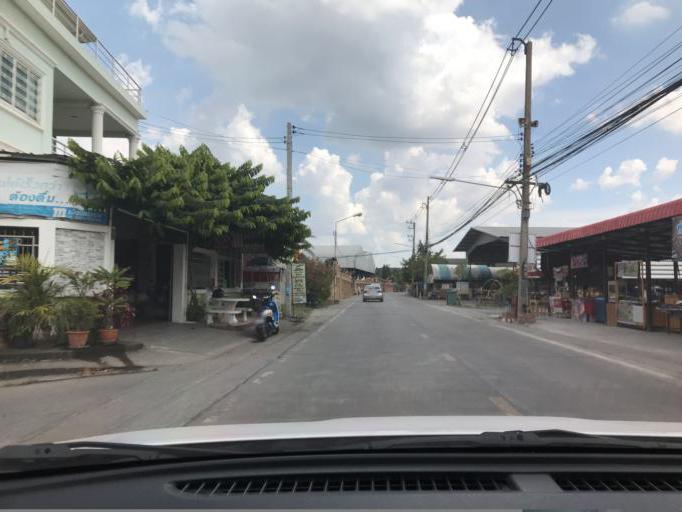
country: TH
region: Phra Nakhon Si Ayutthaya
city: Ban Bang Kadi Pathum Thani
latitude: 14.0033
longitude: 100.5498
